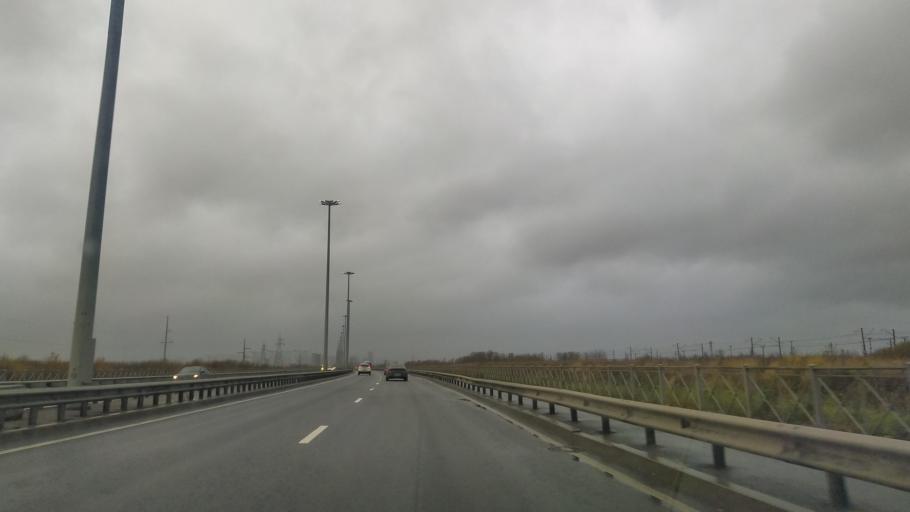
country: RU
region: St.-Petersburg
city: Shushary
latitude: 59.7763
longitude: 30.4012
